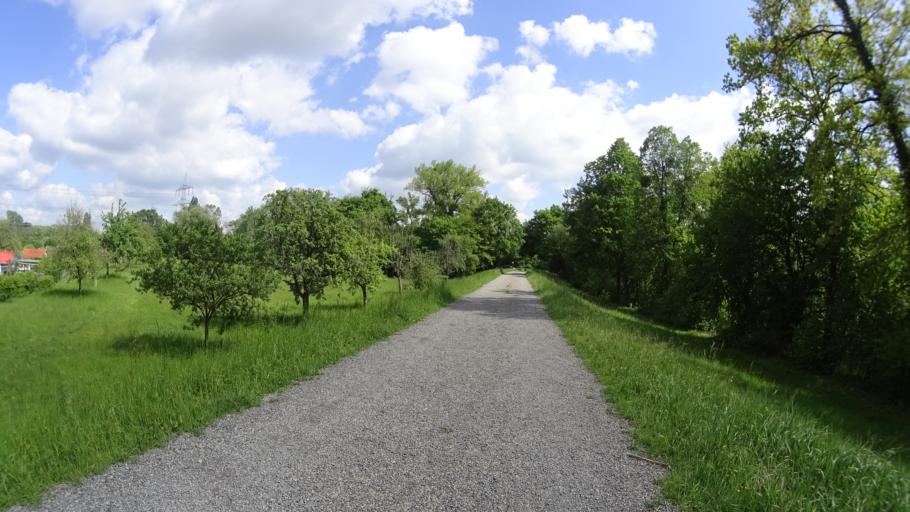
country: DE
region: Baden-Wuerttemberg
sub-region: Karlsruhe Region
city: Rheinstetten
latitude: 49.0020
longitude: 8.3114
